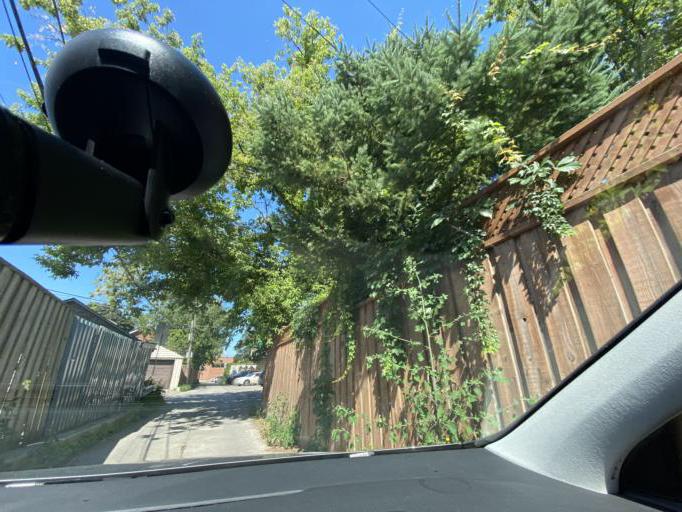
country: CA
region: Ontario
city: Etobicoke
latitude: 43.6652
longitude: -79.4939
